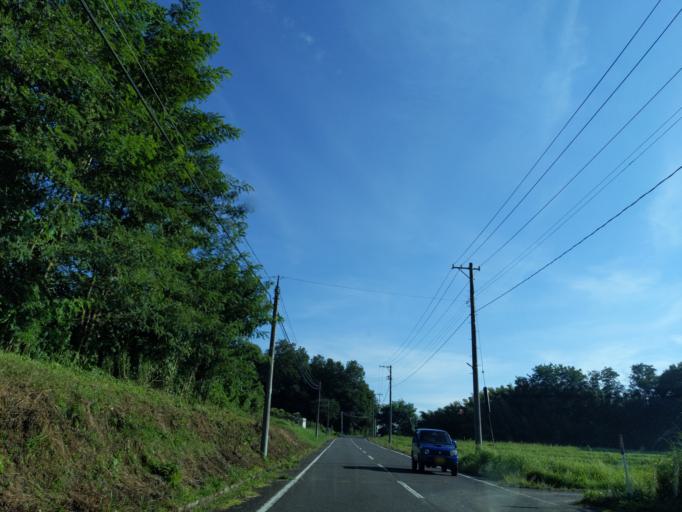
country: JP
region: Fukushima
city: Sukagawa
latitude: 37.3233
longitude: 140.4346
